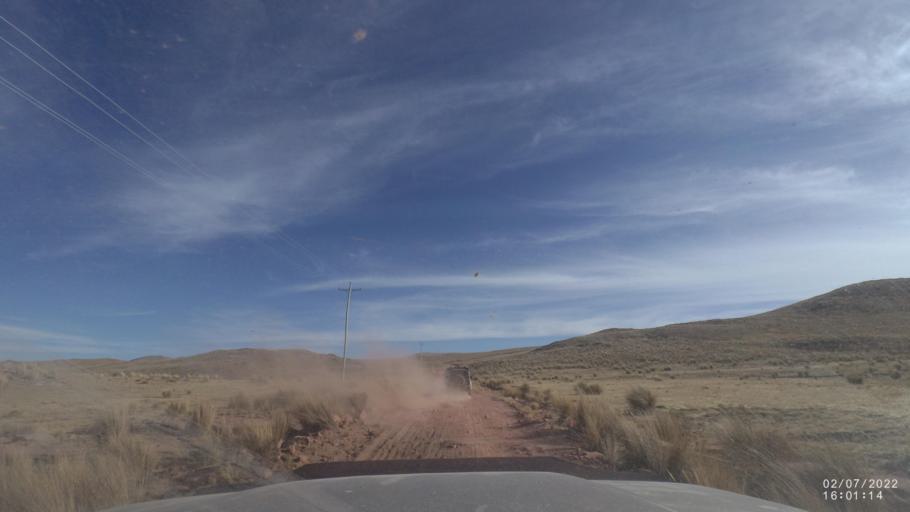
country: BO
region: Cochabamba
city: Irpa Irpa
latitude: -17.9060
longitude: -66.4376
